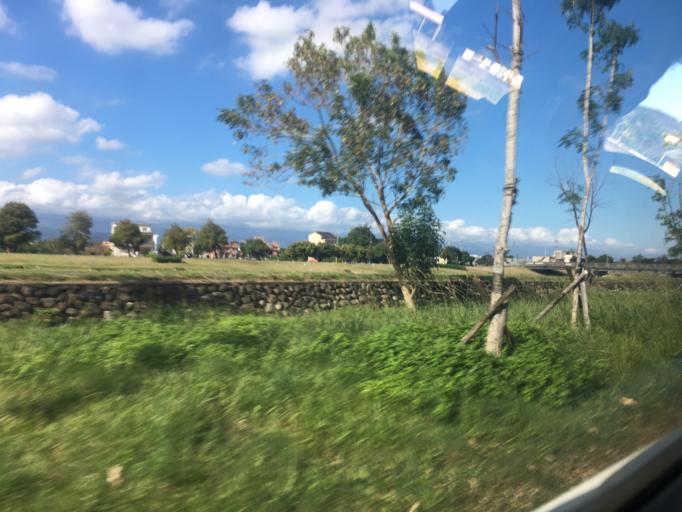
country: TW
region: Taiwan
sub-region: Yilan
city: Yilan
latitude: 24.6951
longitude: 121.7442
